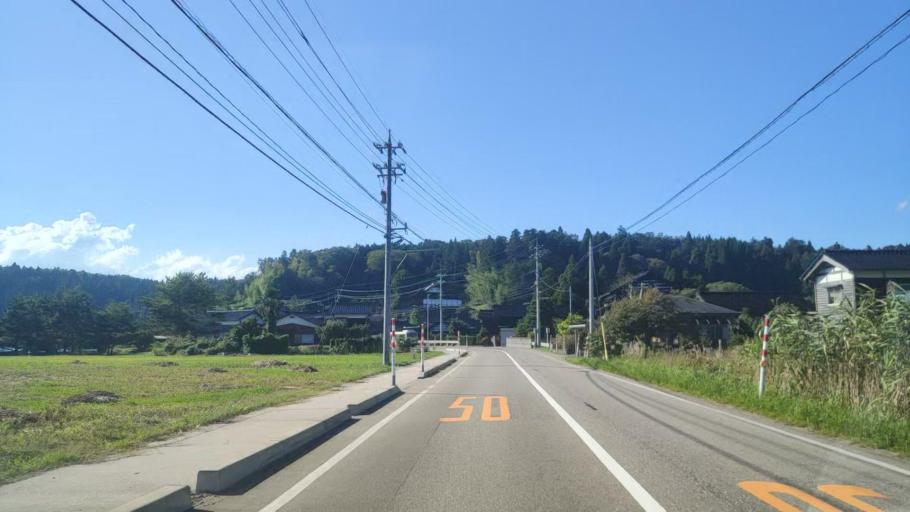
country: JP
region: Ishikawa
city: Nanao
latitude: 37.2360
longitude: 136.9640
